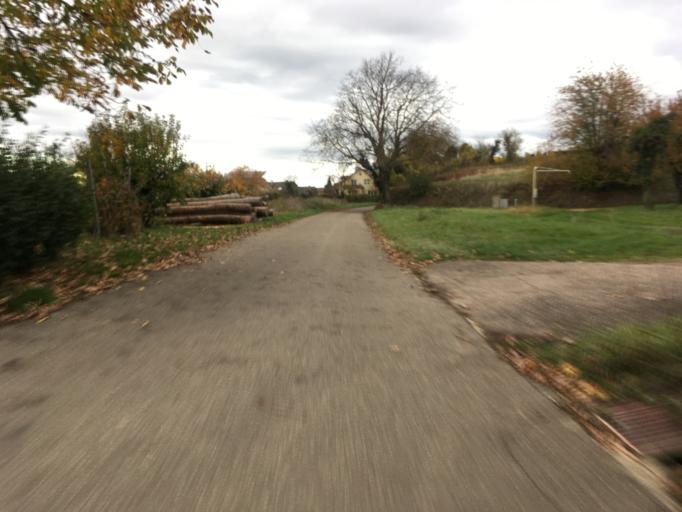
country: DE
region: Baden-Wuerttemberg
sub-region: Freiburg Region
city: Gottenheim
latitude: 48.0429
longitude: 7.7203
